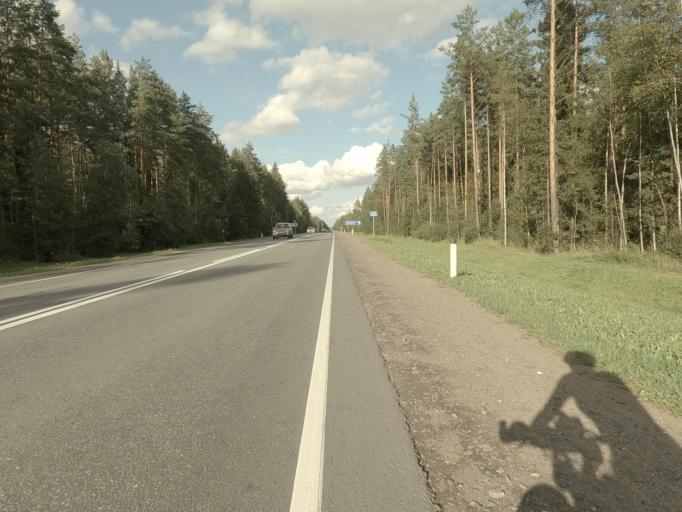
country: RU
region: Leningrad
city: Mga
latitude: 59.6918
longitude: 30.9772
